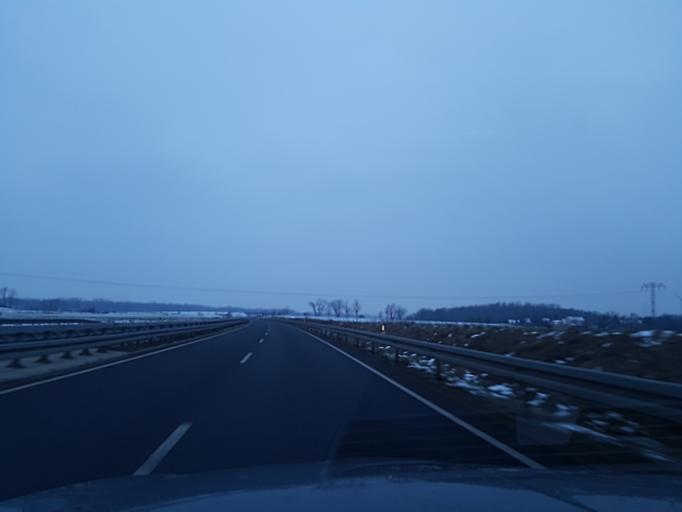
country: DE
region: Saxony
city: Riesa
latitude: 51.2827
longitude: 13.2554
